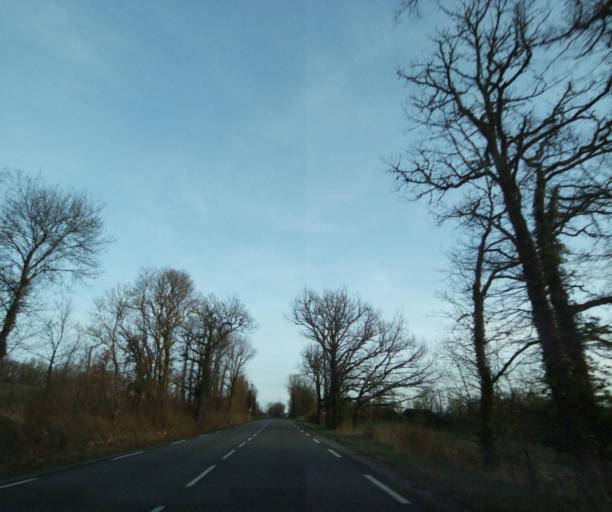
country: FR
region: Midi-Pyrenees
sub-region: Departement du Lot
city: Le Vigan
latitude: 44.6450
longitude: 1.4797
